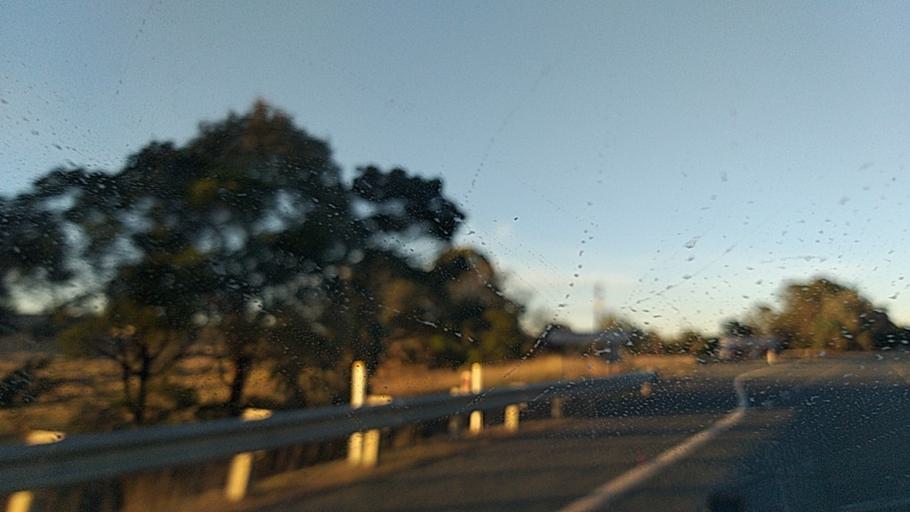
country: AU
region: New South Wales
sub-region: Goulburn Mulwaree
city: Goulburn
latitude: -34.8264
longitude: 149.5975
